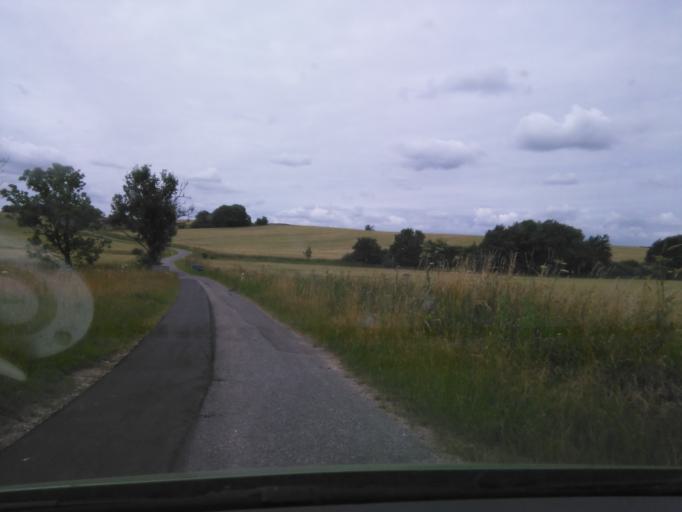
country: DK
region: Central Jutland
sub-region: Arhus Kommune
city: Solbjerg
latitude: 55.9961
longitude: 10.0499
